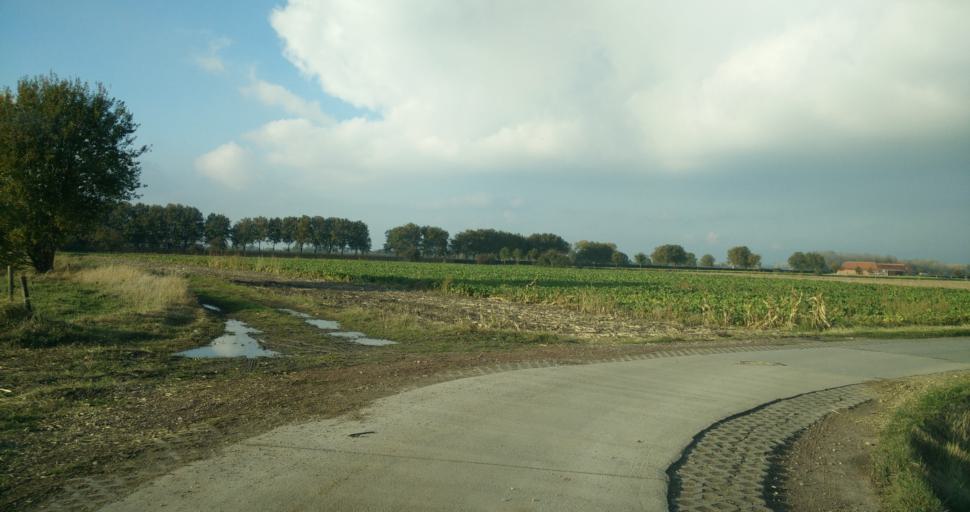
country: BE
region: Flanders
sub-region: Provincie Oost-Vlaanderen
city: Oosterzele
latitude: 50.9179
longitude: 3.7743
